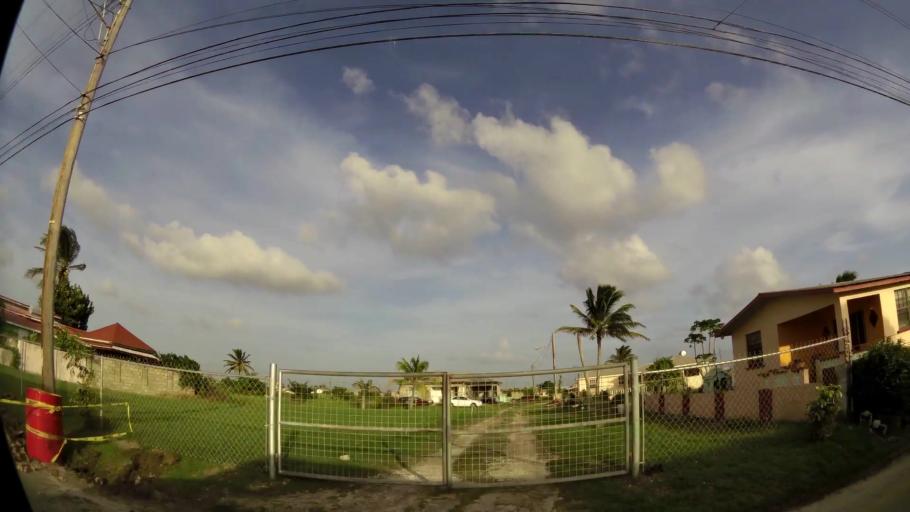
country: BB
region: Christ Church
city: Oistins
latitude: 13.0557
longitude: -59.5110
